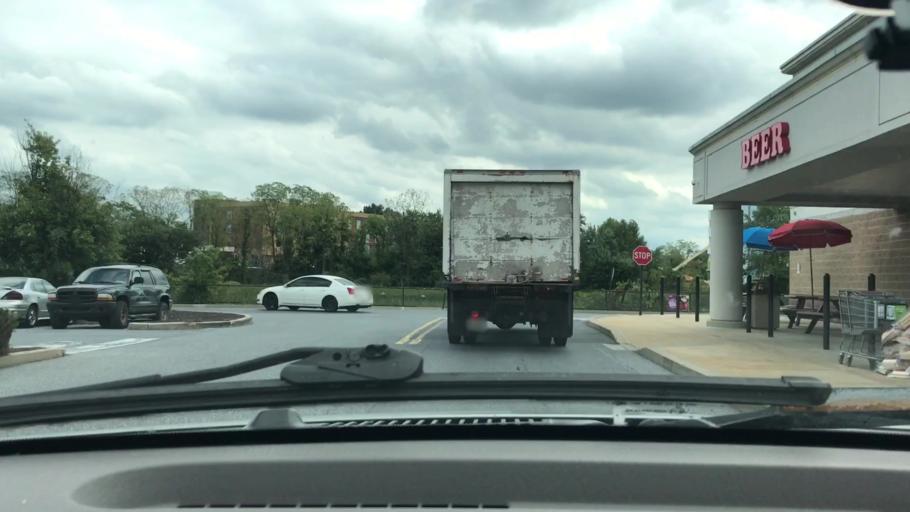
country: US
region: Pennsylvania
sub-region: Lancaster County
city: Lancaster
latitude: 40.0669
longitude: -76.3184
